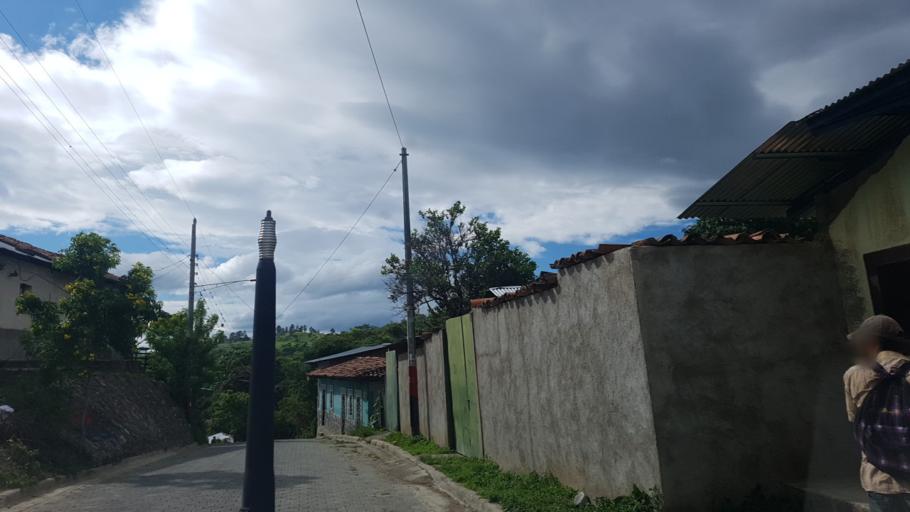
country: HN
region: El Paraiso
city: Oropoli
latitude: 13.7467
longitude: -86.7080
